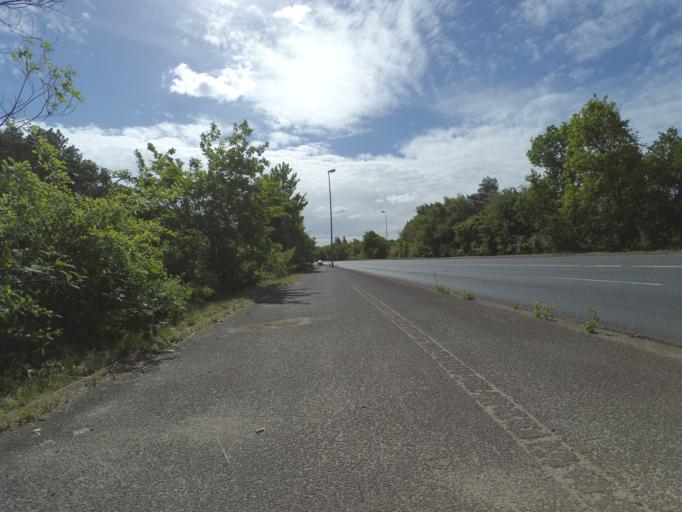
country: DE
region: Lower Saxony
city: Auf der Horst
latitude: 52.4145
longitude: 9.6197
